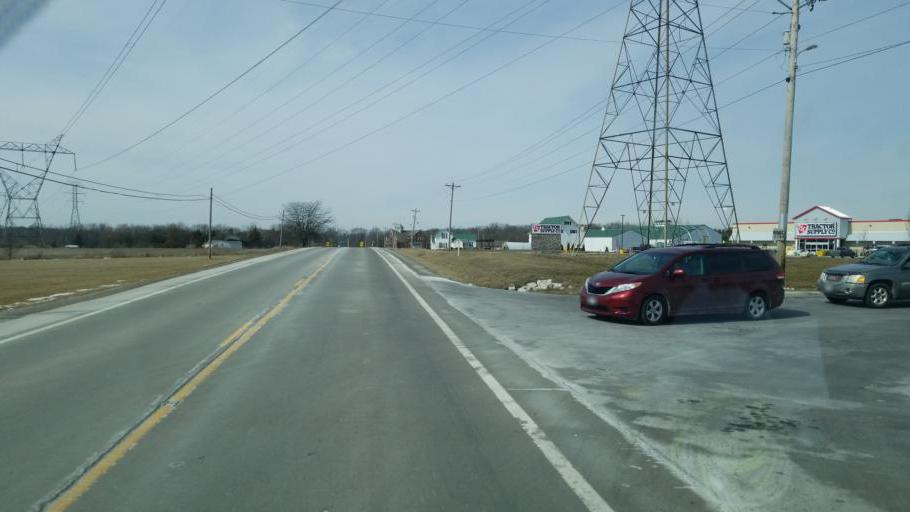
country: US
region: Ohio
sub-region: Delaware County
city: Sunbury
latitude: 40.2590
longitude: -82.8847
